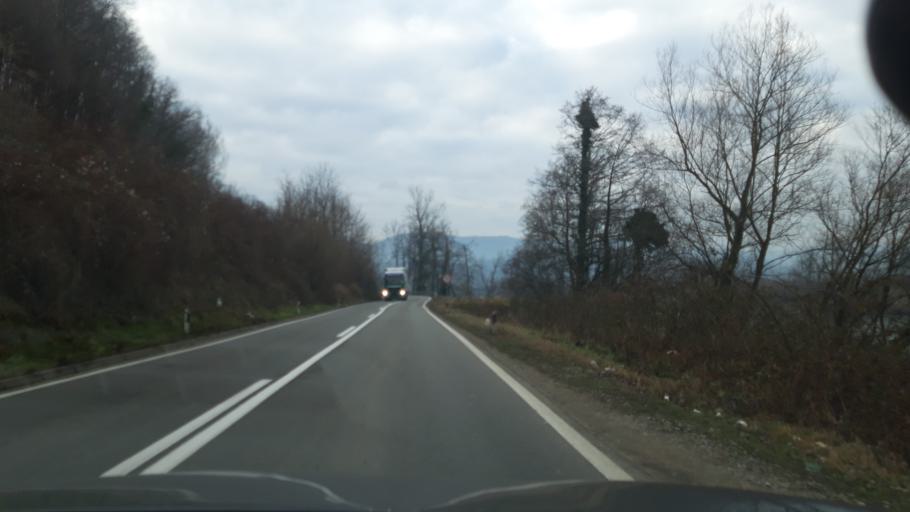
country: BA
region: Republika Srpska
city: Zvornik
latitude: 44.4190
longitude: 19.1484
